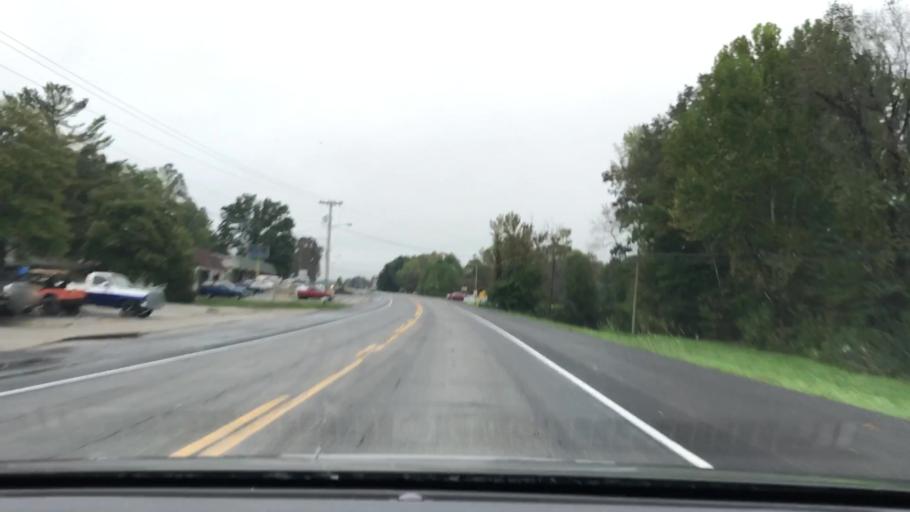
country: US
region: Tennessee
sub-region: Scott County
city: Oneida
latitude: 36.5526
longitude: -84.4520
